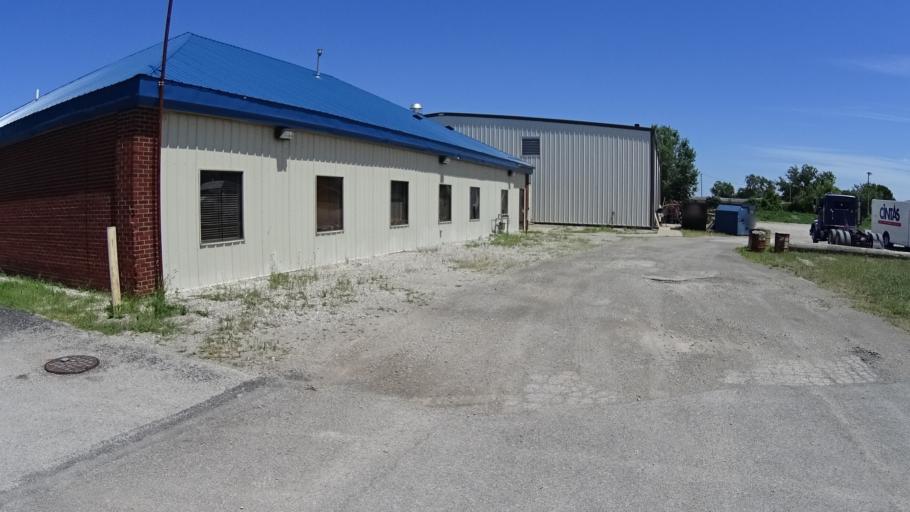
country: US
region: Ohio
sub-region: Erie County
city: Sandusky
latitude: 41.4317
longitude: -82.7027
